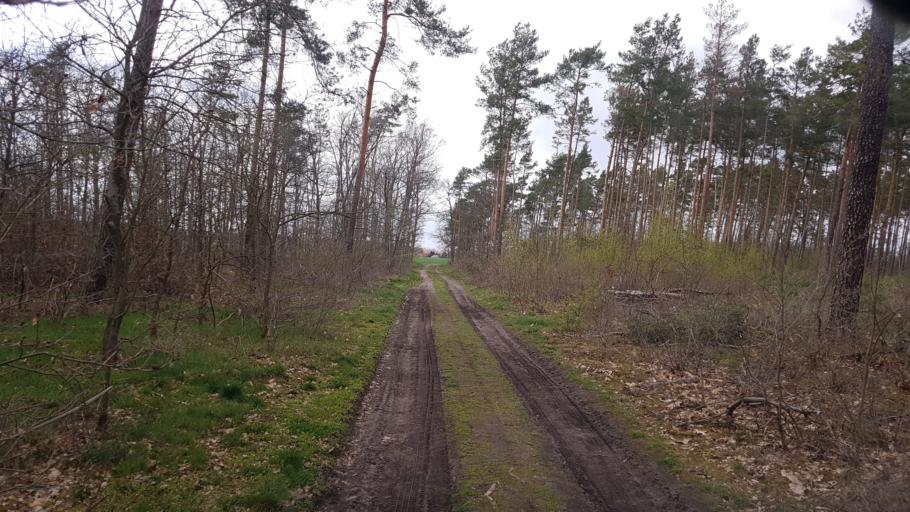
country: DE
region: Brandenburg
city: Calau
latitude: 51.7364
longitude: 13.9290
